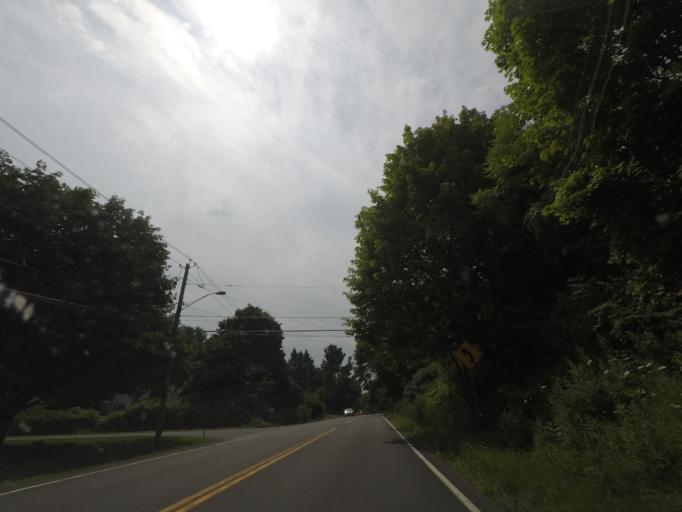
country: US
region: New York
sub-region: Saratoga County
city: Waterford
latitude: 42.7722
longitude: -73.6398
